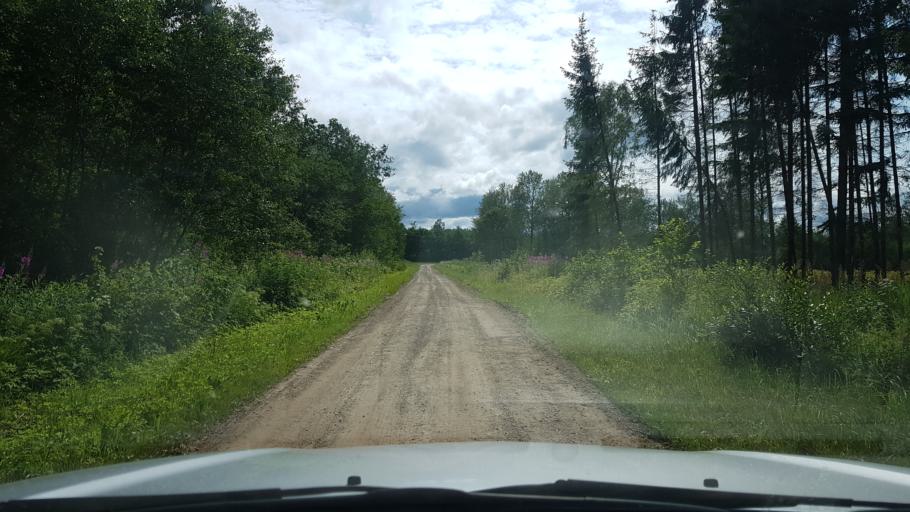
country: EE
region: Ida-Virumaa
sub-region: Narva-Joesuu linn
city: Narva-Joesuu
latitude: 59.3650
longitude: 27.9233
